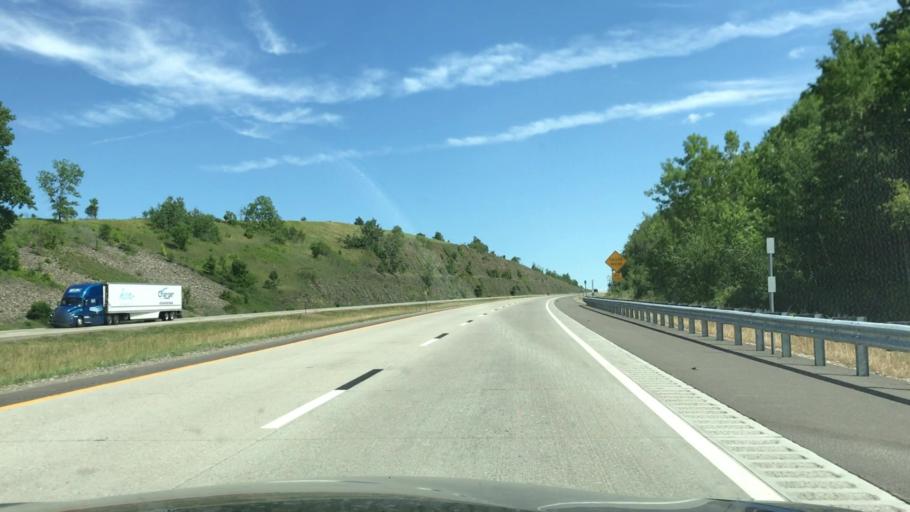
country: US
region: New York
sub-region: Steuben County
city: Wayland
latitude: 42.5340
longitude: -77.5597
